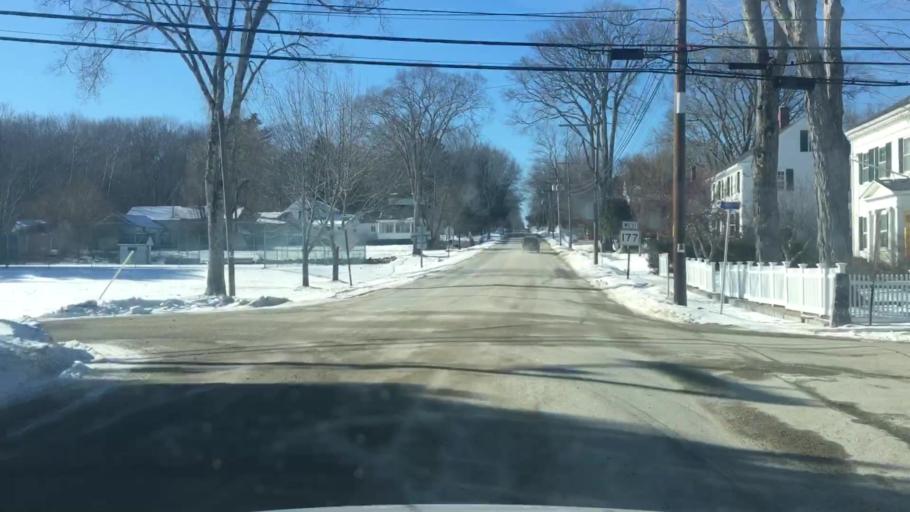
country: US
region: Maine
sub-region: Hancock County
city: Sedgwick
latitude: 44.4132
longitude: -68.5908
